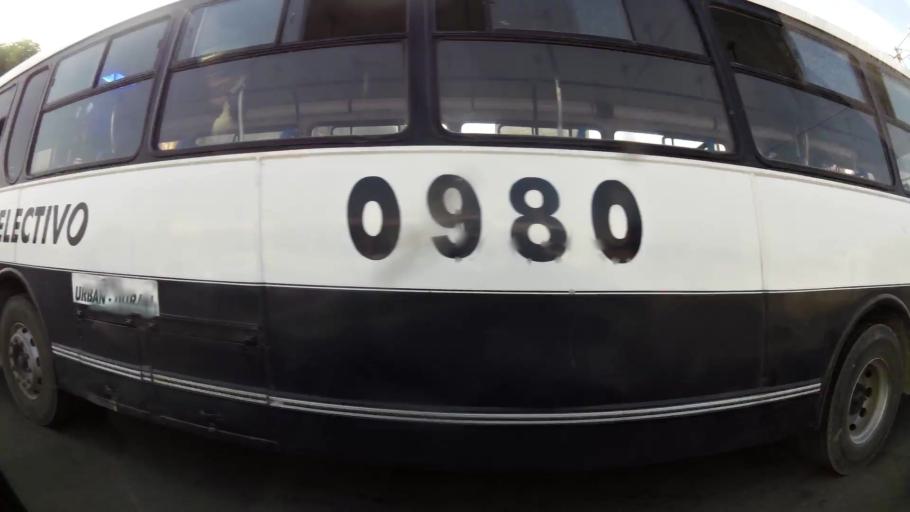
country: EC
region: Guayas
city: Eloy Alfaro
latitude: -2.1850
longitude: -79.8494
